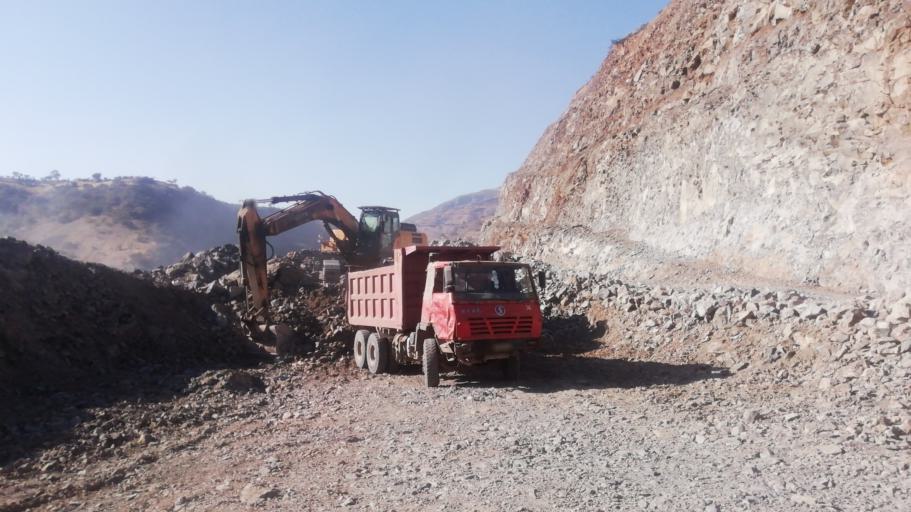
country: ET
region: Amhara
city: Addiet Canna
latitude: 11.2229
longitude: 37.8716
